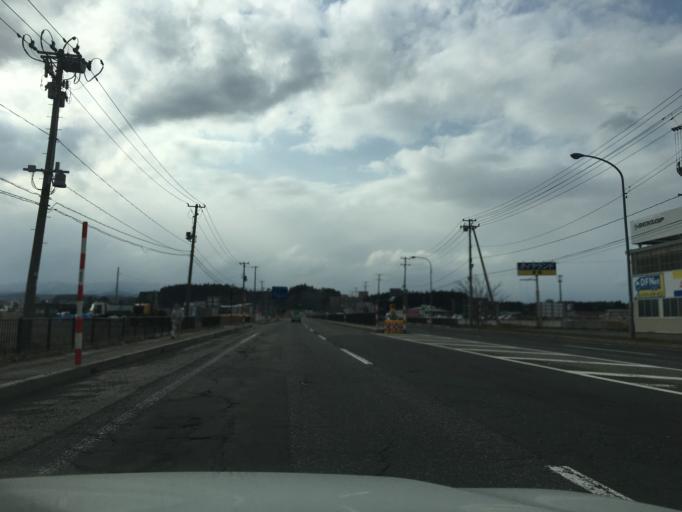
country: JP
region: Aomori
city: Aomori Shi
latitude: 40.8339
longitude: 140.6858
